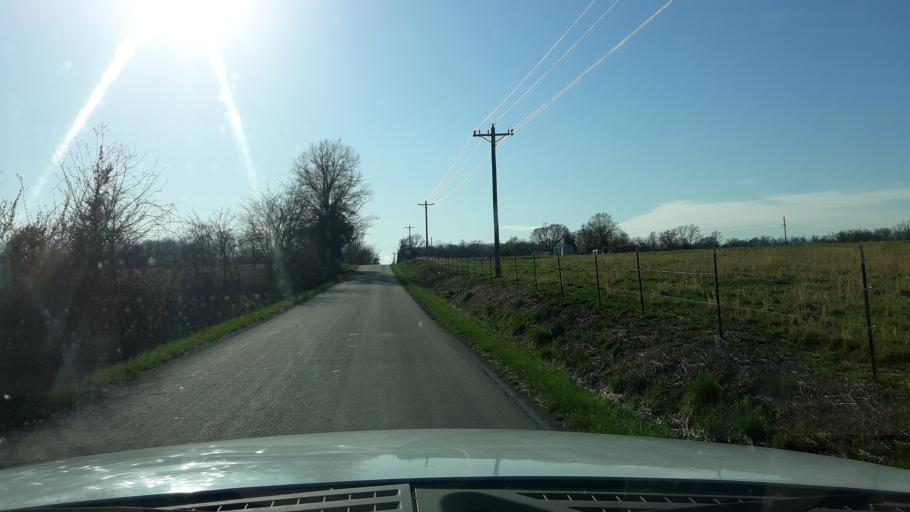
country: US
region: Illinois
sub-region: Saline County
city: Harrisburg
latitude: 37.8048
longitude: -88.6104
